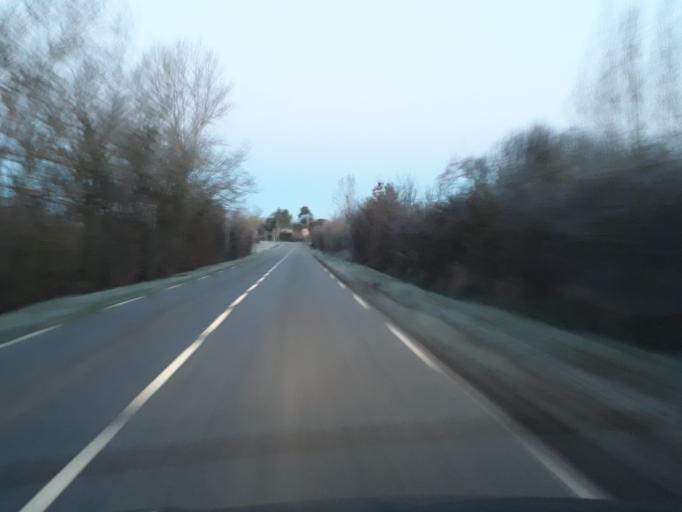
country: FR
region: Midi-Pyrenees
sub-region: Departement du Gers
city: Samatan
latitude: 43.4745
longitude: 0.9547
